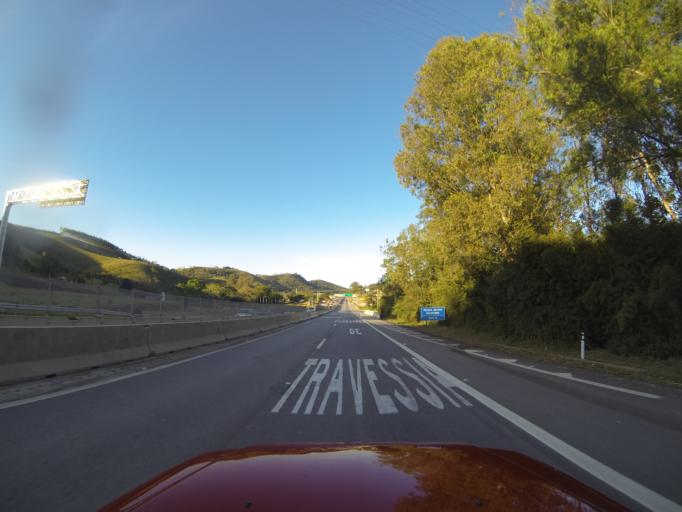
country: BR
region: Sao Paulo
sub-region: Santa Branca
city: Santa Branca
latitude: -23.3227
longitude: -45.7399
